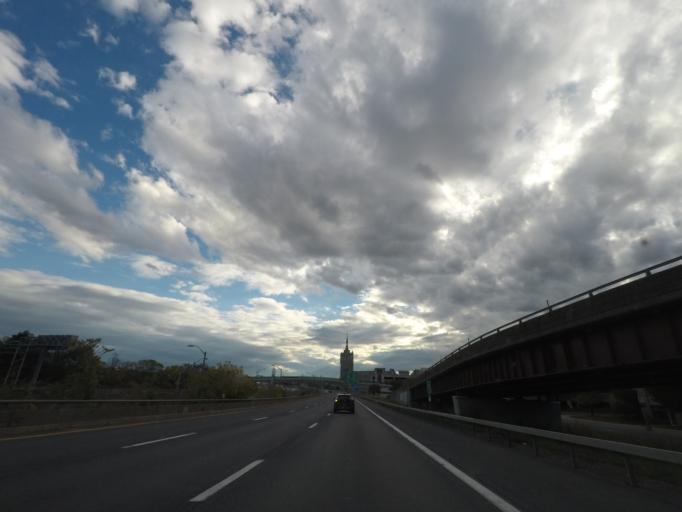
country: US
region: New York
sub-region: Albany County
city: Albany
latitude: 42.6523
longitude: -73.7474
